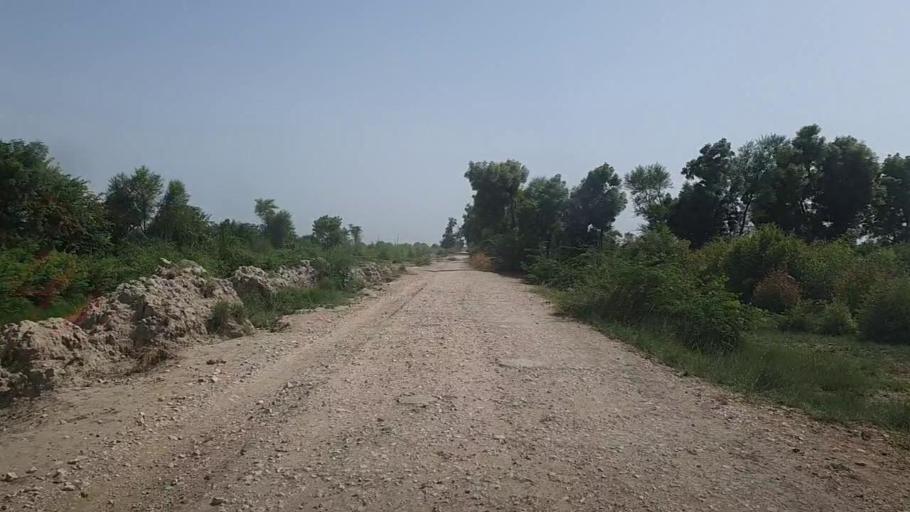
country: PK
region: Sindh
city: Pad Idan
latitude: 26.7852
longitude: 68.3248
